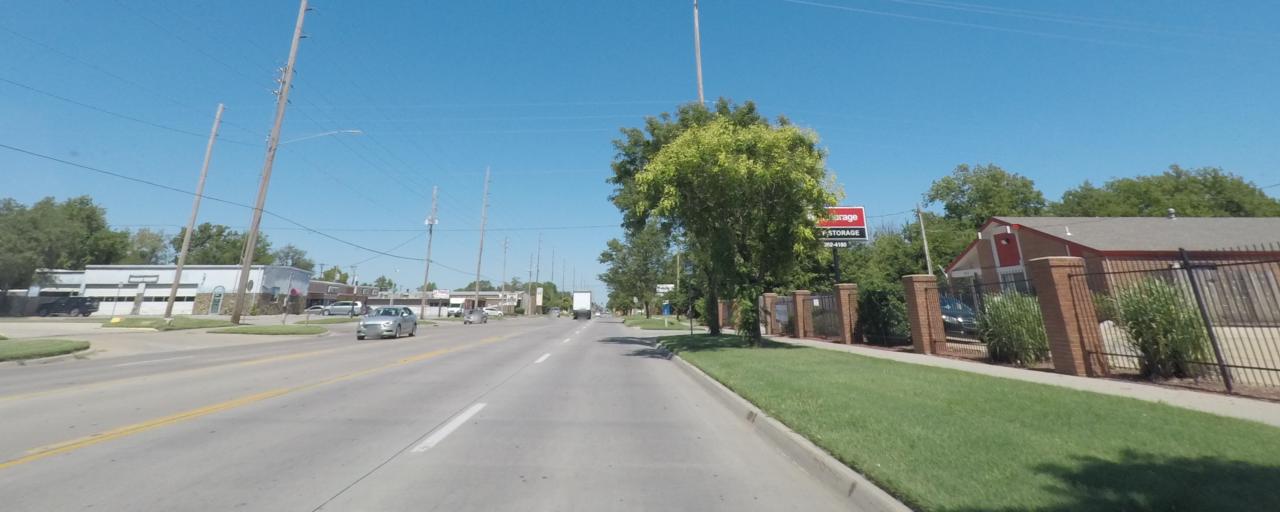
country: US
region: Kansas
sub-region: Sedgwick County
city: Wichita
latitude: 37.6583
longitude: -97.3528
